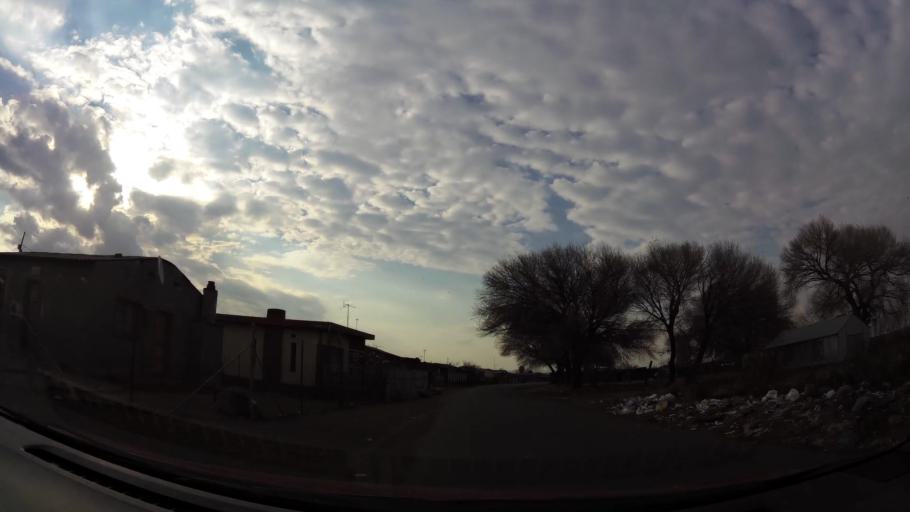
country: ZA
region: Gauteng
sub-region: Sedibeng District Municipality
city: Vanderbijlpark
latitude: -26.6915
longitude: 27.8770
